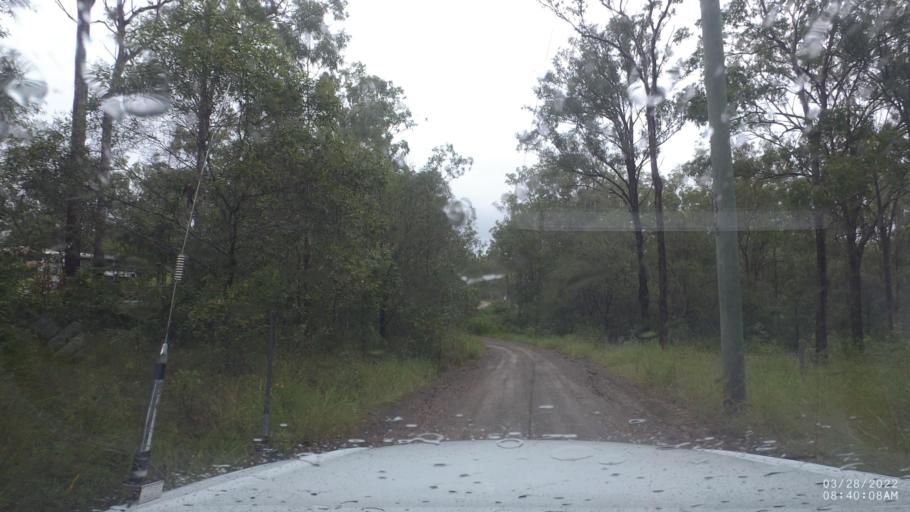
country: AU
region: Queensland
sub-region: Logan
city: Cedar Vale
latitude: -27.8372
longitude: 153.0645
